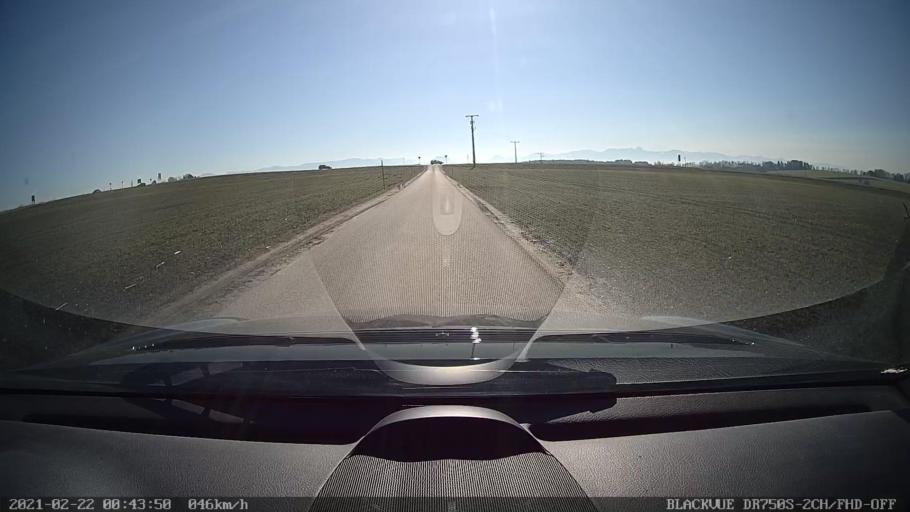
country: DE
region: Bavaria
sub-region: Upper Bavaria
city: Griesstatt
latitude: 47.9891
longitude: 12.1721
